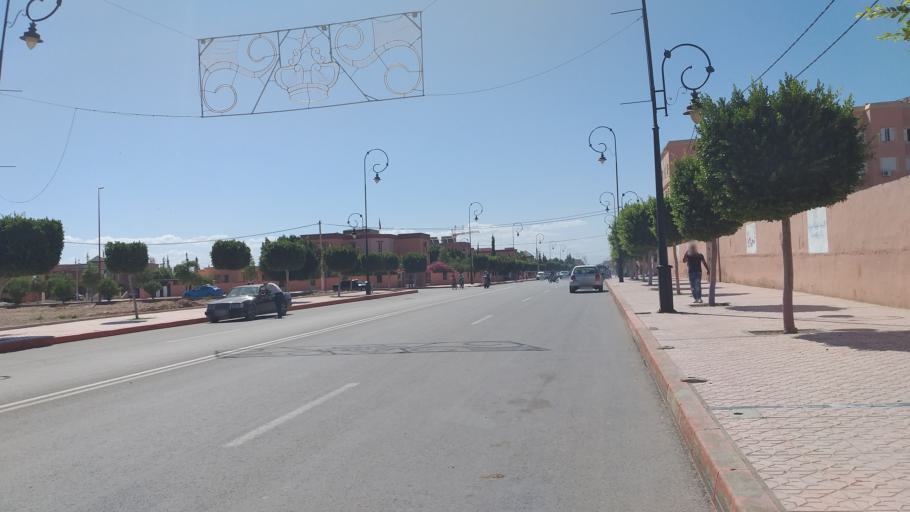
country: MA
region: Marrakech-Tensift-Al Haouz
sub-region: Chichaoua
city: Chichaoua
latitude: 31.5409
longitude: -8.7674
